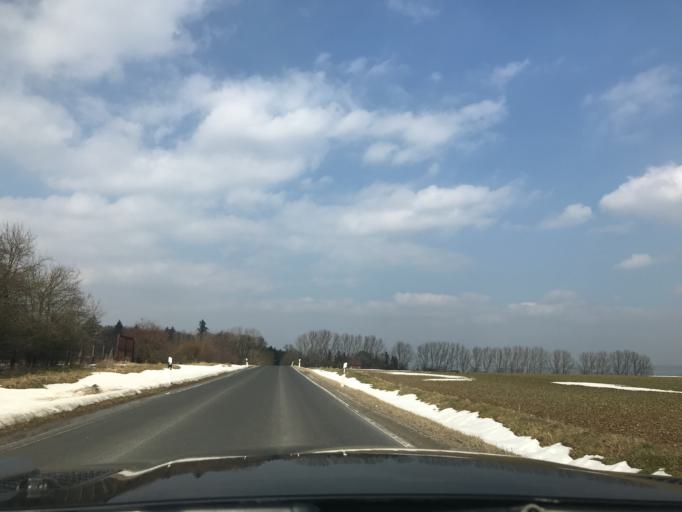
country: DE
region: Thuringia
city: Oberdorla
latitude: 51.1721
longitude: 10.3971
